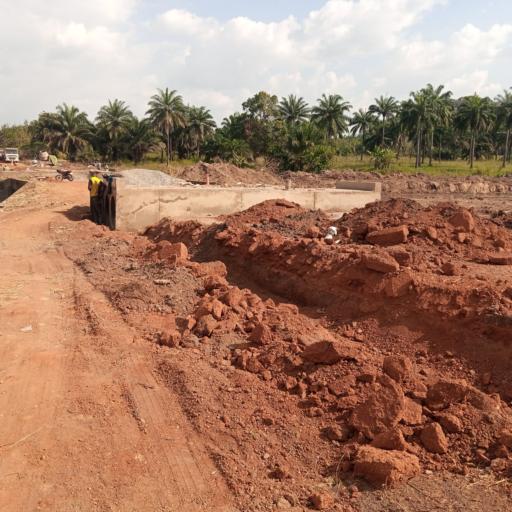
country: NG
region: Osun
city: Bode Osi
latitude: 7.7506
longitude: 4.1221
